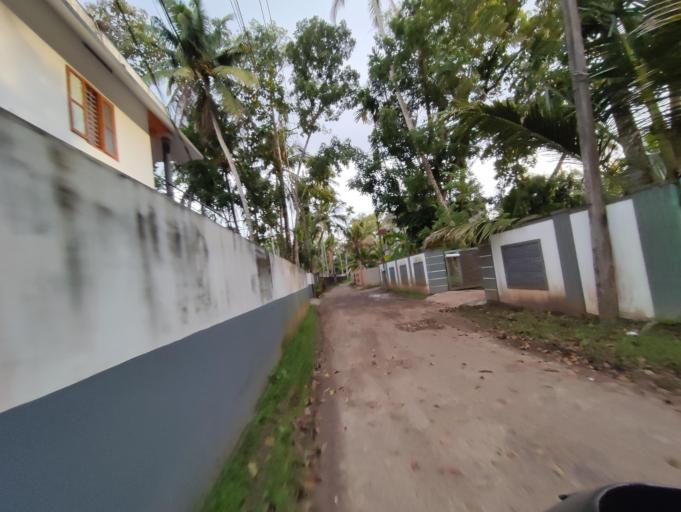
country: IN
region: Kerala
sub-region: Alappuzha
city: Vayalar
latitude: 9.6972
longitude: 76.3348
